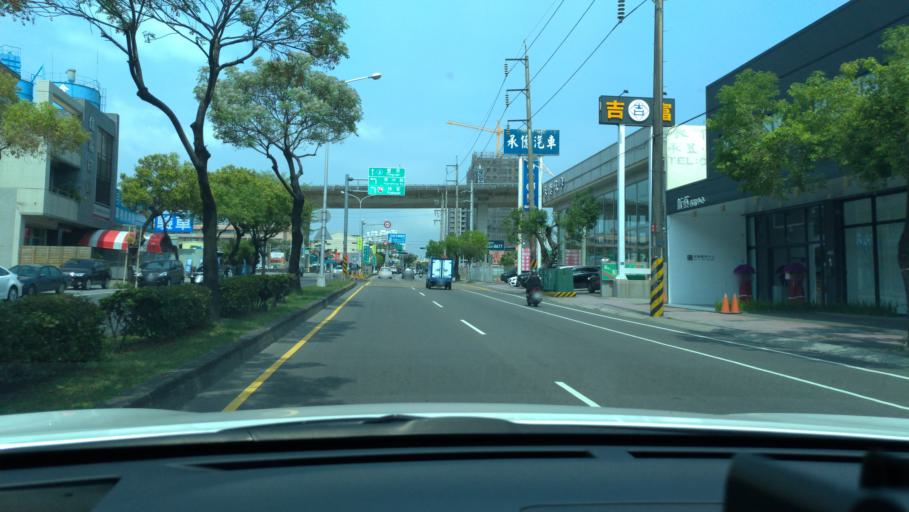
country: TW
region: Taiwan
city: Fengyuan
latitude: 24.1992
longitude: 120.7032
